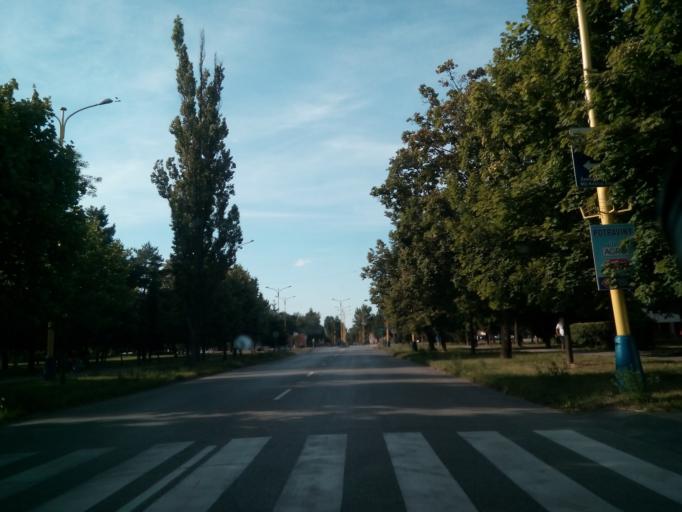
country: SK
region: Kosicky
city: Kosice
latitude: 48.6321
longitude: 21.1724
